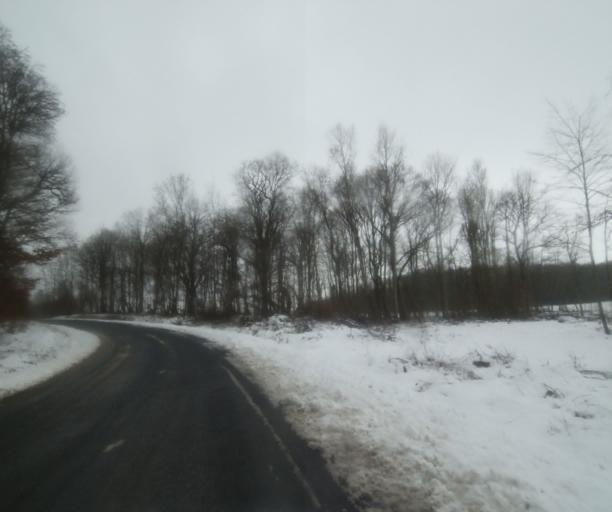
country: FR
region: Champagne-Ardenne
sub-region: Departement de la Haute-Marne
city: Montier-en-Der
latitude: 48.4679
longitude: 4.8155
